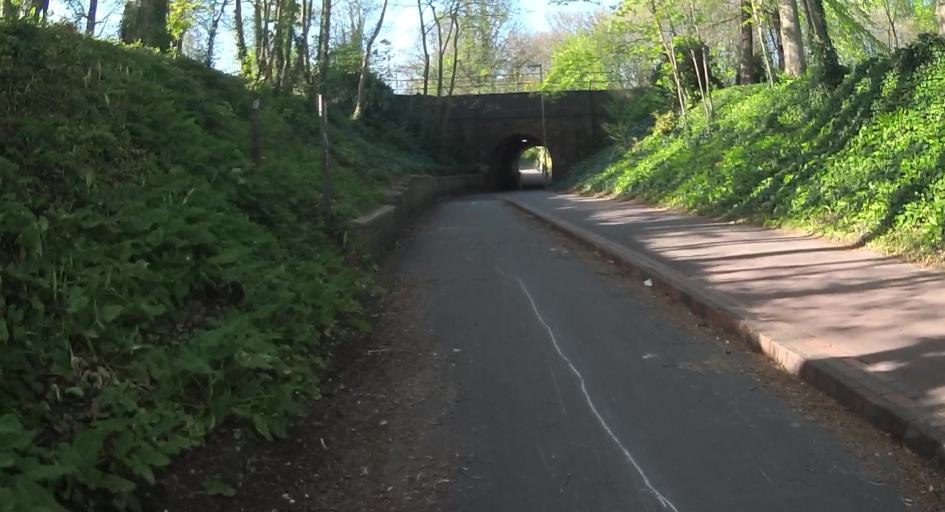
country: GB
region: England
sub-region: Hampshire
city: Basingstoke
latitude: 51.2664
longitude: -1.1128
